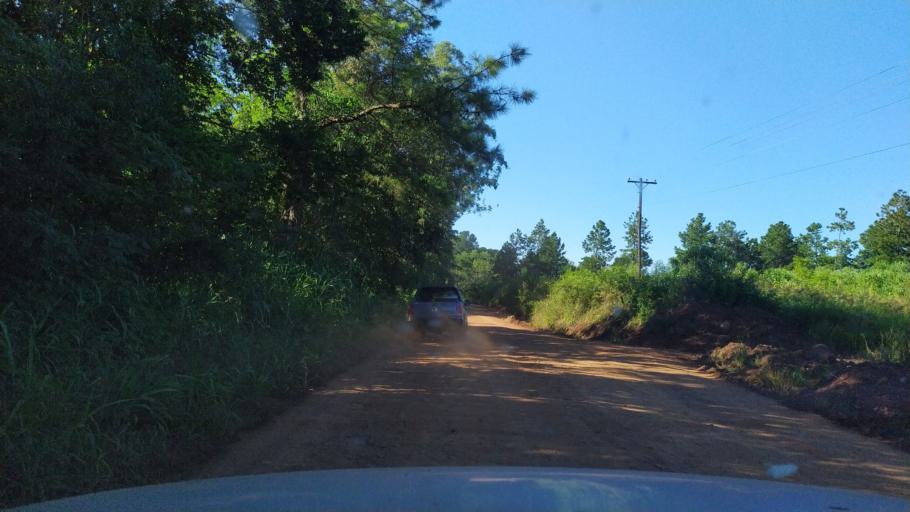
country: AR
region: Misiones
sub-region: Departamento de Montecarlo
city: Montecarlo
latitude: -26.6212
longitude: -54.6960
